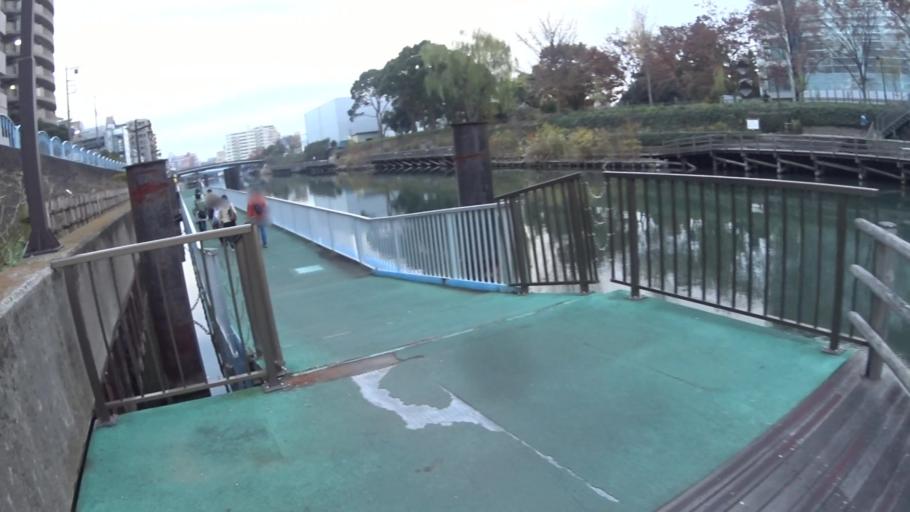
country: JP
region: Tokyo
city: Urayasu
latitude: 35.6887
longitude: 139.8203
